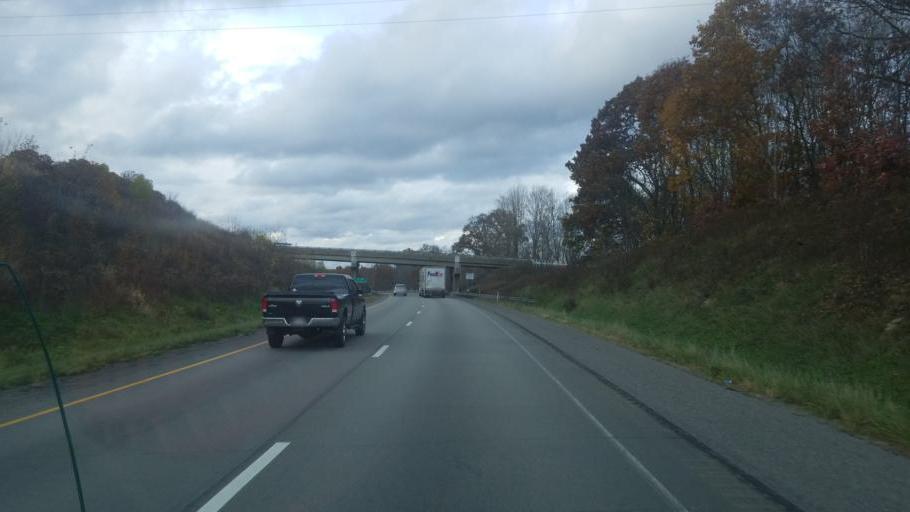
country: US
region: Pennsylvania
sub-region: Venango County
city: Franklin
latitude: 41.1913
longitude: -79.7999
